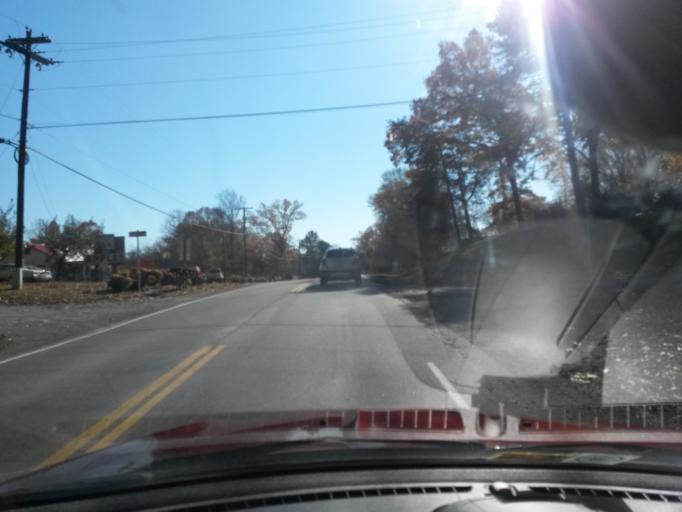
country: US
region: Virginia
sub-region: City of Bedford
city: Bedford
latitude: 37.3794
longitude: -79.5498
